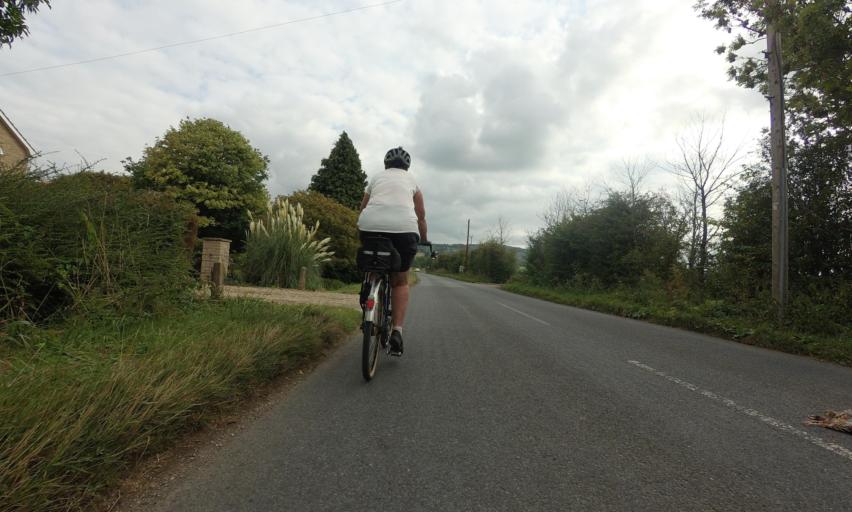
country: GB
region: England
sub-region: Gloucestershire
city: Winchcombe
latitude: 51.9825
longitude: -1.9979
